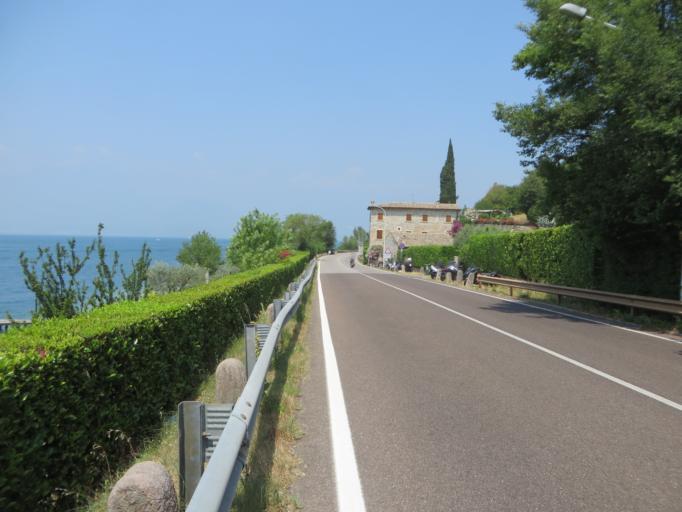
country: IT
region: Veneto
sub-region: Provincia di Verona
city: Torri del Benaco
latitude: 45.5832
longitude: 10.6743
